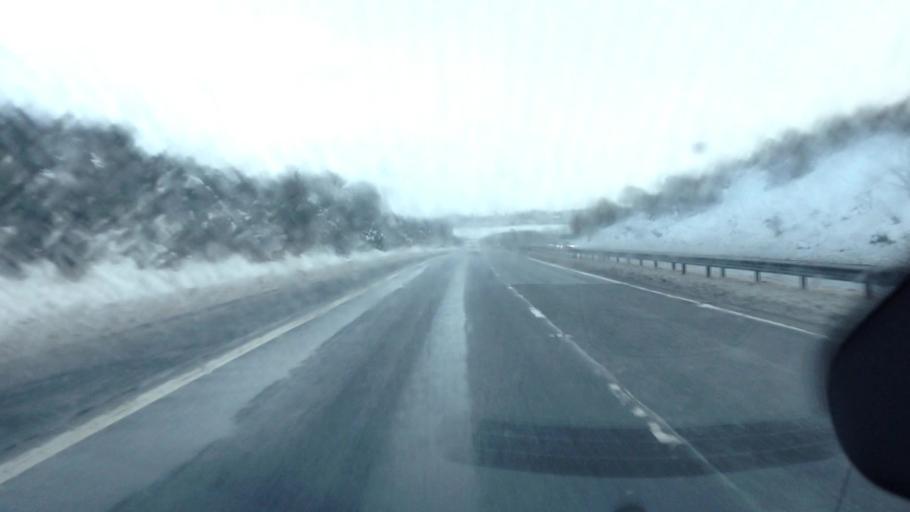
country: GB
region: Scotland
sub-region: South Lanarkshire
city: Blackwood
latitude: 55.6570
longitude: -3.9054
